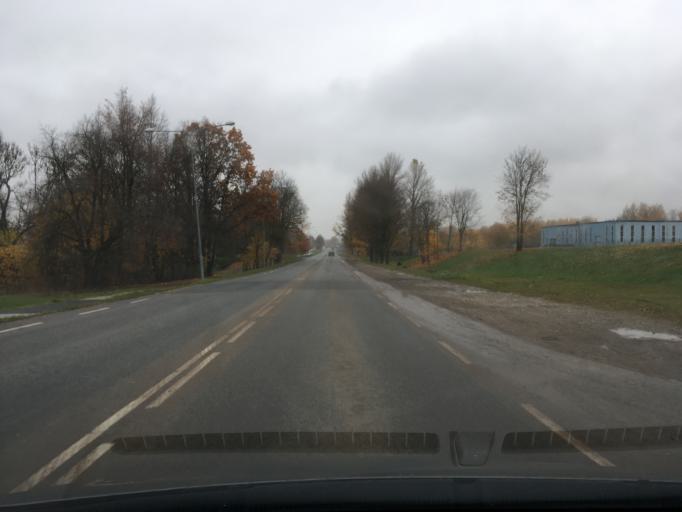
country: EE
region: Tartu
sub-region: Tartu linn
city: Tartu
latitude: 58.4010
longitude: 26.7084
